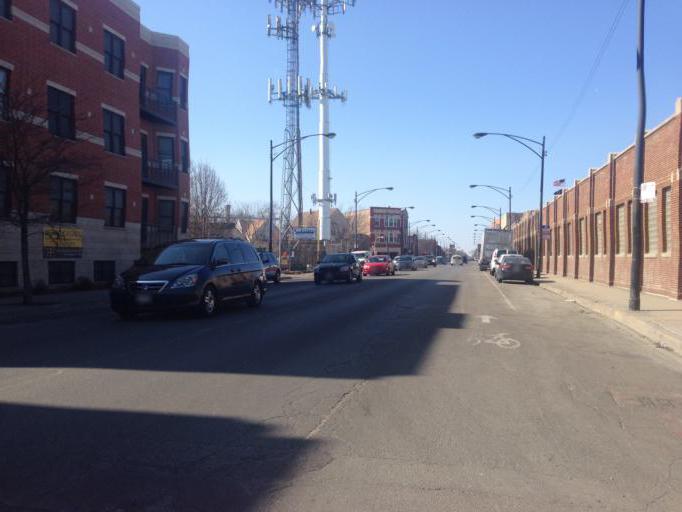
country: US
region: Illinois
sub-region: Cook County
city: Lincolnwood
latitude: 41.9435
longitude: -87.7042
